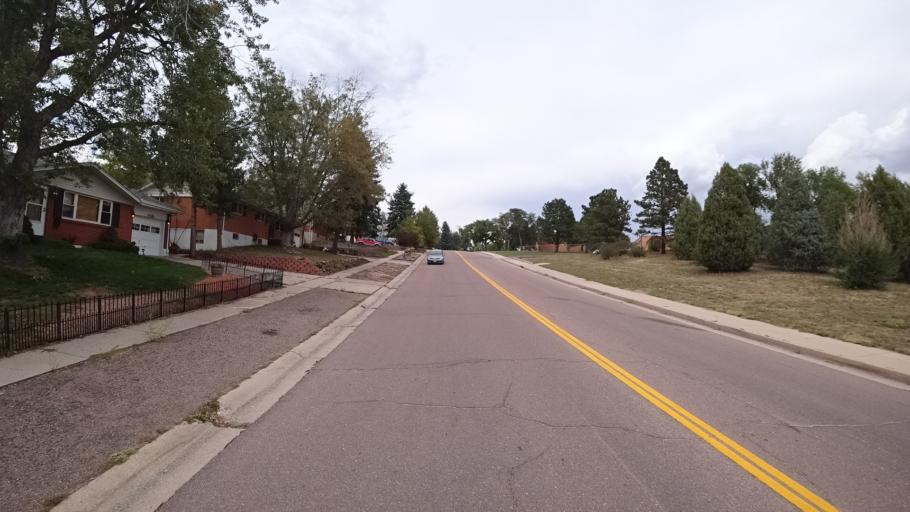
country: US
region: Colorado
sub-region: El Paso County
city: Colorado Springs
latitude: 38.8596
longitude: -104.7840
